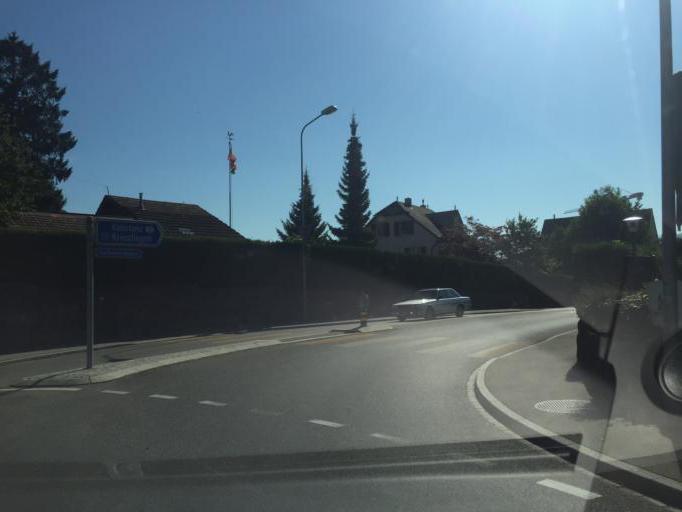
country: CH
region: Schaffhausen
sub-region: Bezirk Stein
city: Stein am Rhein
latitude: 47.6558
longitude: 8.8580
